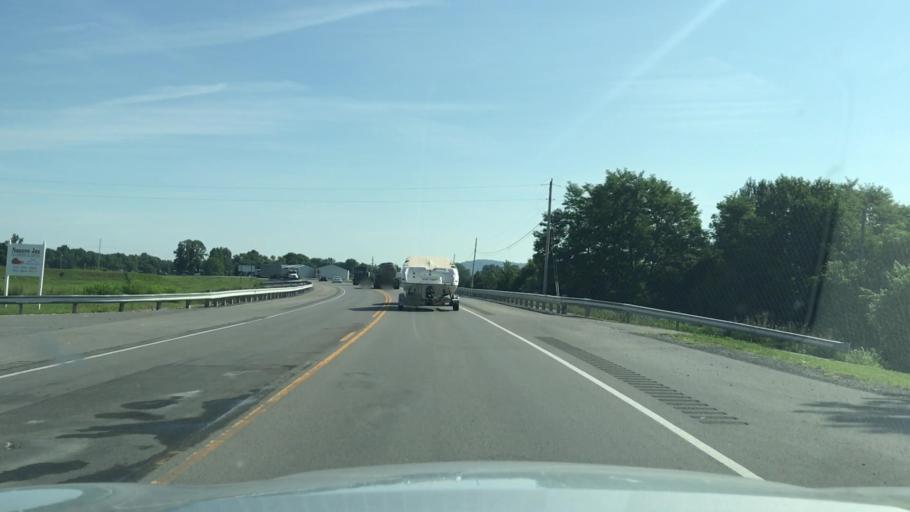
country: US
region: Tennessee
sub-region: Pickett County
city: Byrdstown
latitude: 36.6176
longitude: -85.0902
